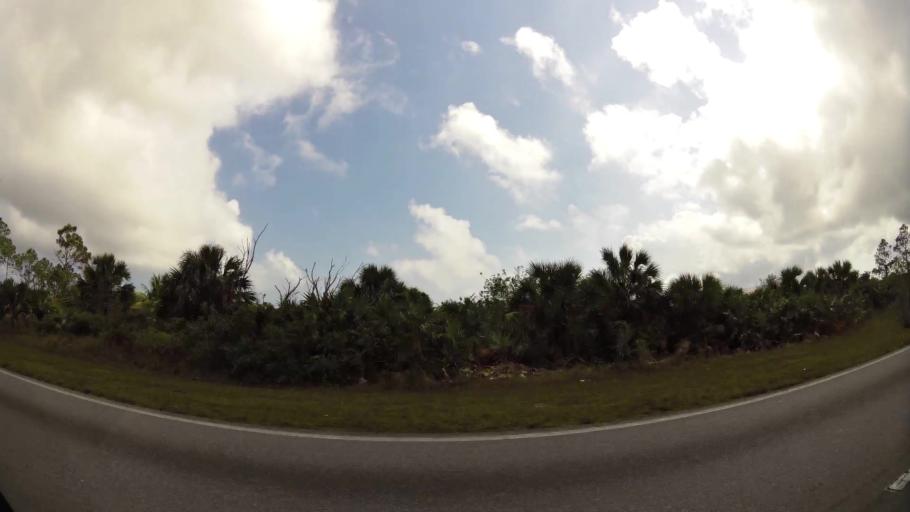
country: BS
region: Freeport
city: Freeport
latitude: 26.5172
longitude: -78.7123
